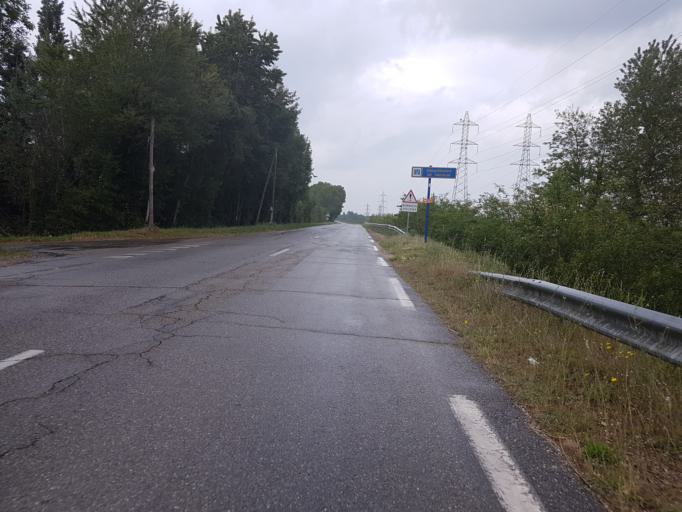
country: FR
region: Languedoc-Roussillon
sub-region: Departement du Gard
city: Villeneuve-les-Avignon
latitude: 43.9863
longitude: 4.8216
